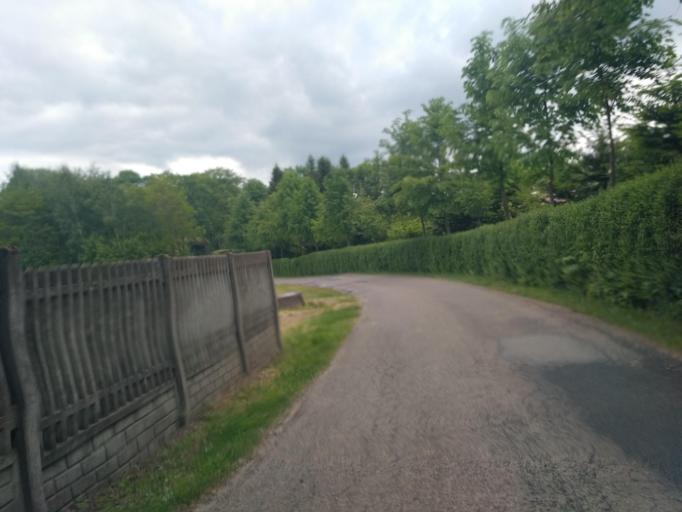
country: PL
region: Subcarpathian Voivodeship
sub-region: Powiat krosnienski
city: Jedlicze
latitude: 49.7184
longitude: 21.6876
